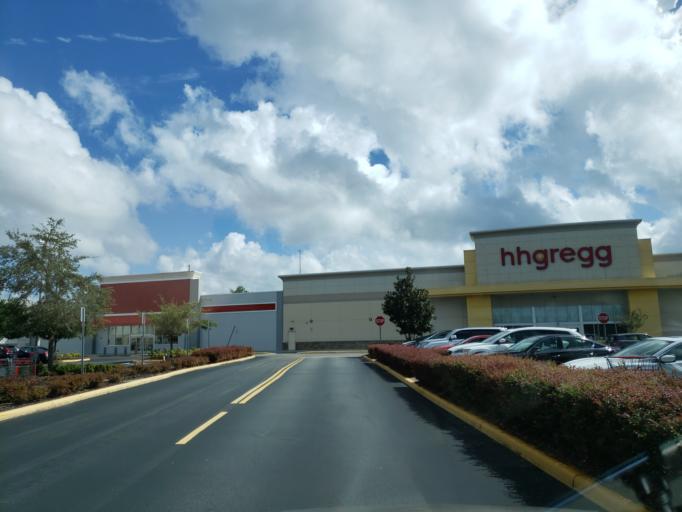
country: US
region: Florida
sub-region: Hillsborough County
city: Pebble Creek
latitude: 28.1169
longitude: -82.3750
